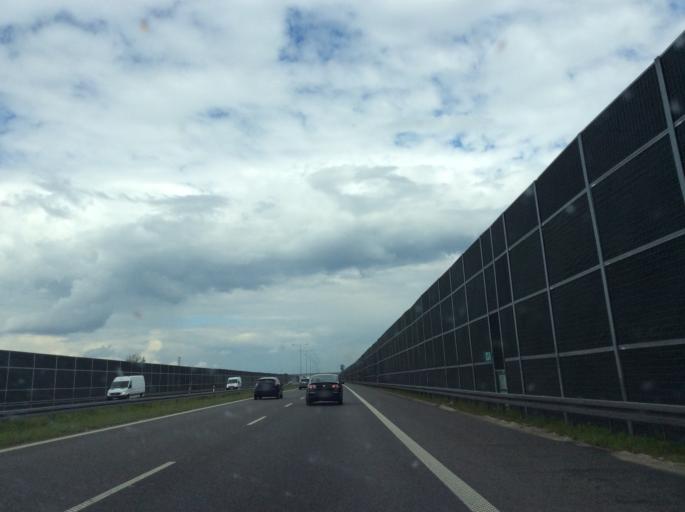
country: PL
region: Masovian Voivodeship
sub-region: Powiat grodziski
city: Milanowek
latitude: 52.1529
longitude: 20.6722
